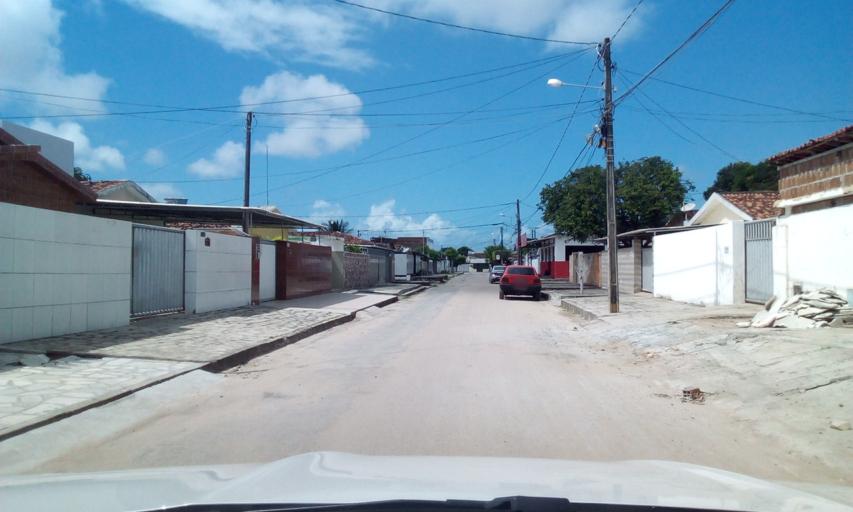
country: BR
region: Paraiba
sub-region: Joao Pessoa
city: Joao Pessoa
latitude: -7.1792
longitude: -34.8708
